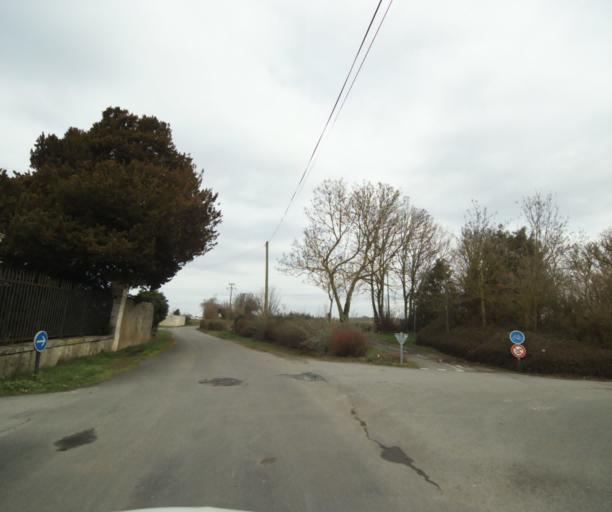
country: FR
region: Poitou-Charentes
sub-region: Departement de la Charente-Maritime
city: Lagord
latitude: 46.1909
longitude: -1.1668
